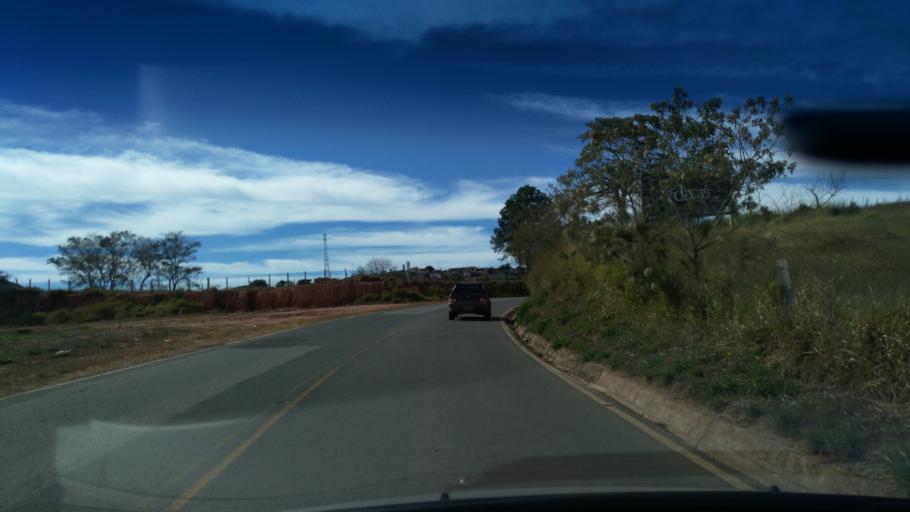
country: BR
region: Minas Gerais
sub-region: Andradas
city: Andradas
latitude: -22.0668
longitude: -46.4482
